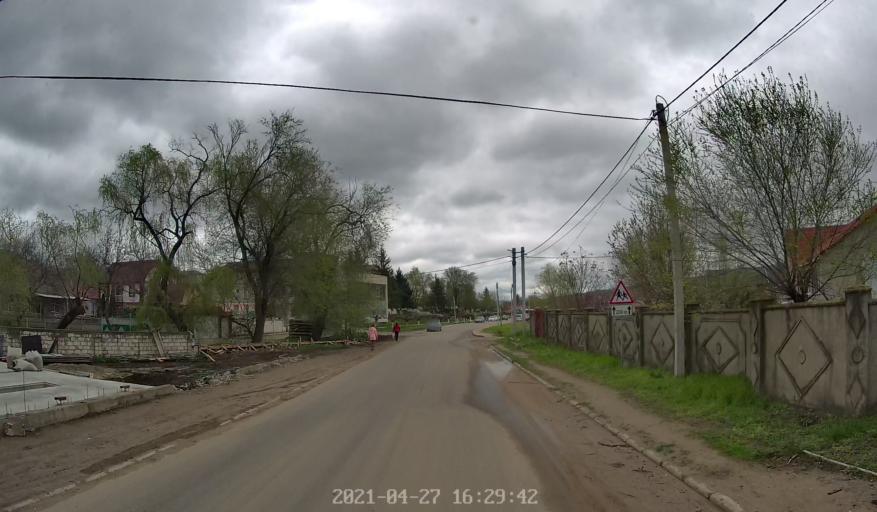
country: MD
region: Chisinau
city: Singera
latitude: 46.9663
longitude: 29.0529
